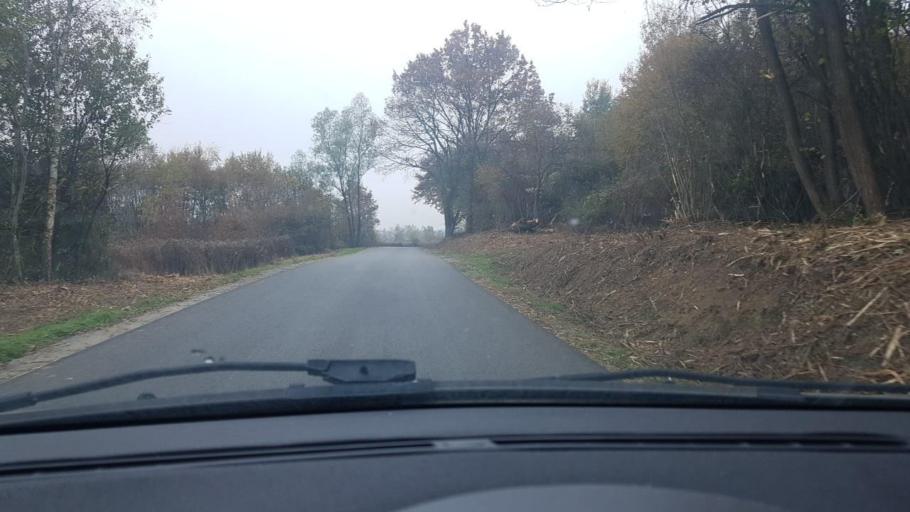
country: HR
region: Krapinsko-Zagorska
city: Marija Bistrica
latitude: 46.0776
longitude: 16.1848
